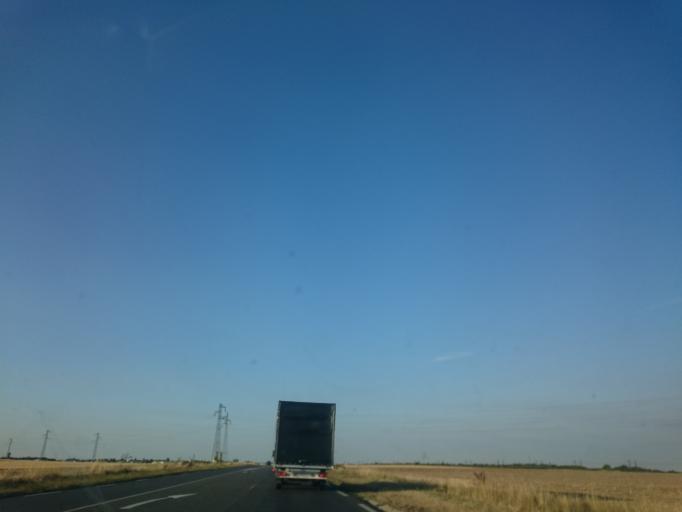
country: FR
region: Centre
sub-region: Departement d'Eure-et-Loir
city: Toury
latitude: 48.1705
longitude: 1.9211
